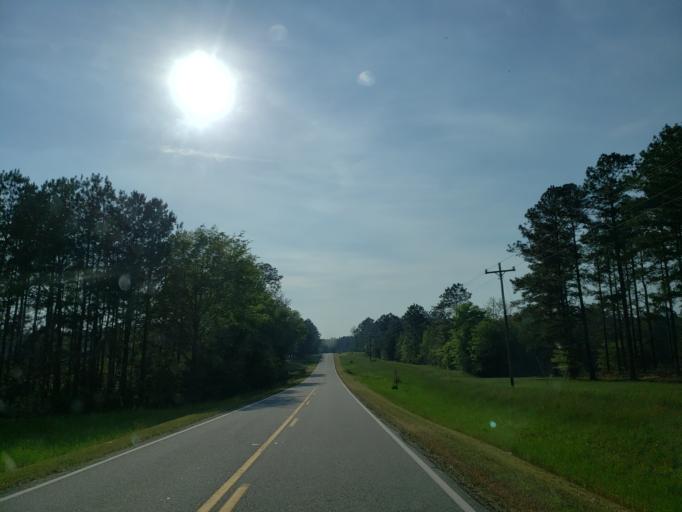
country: US
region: Georgia
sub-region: Tift County
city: Tifton
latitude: 31.5586
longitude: -83.4969
